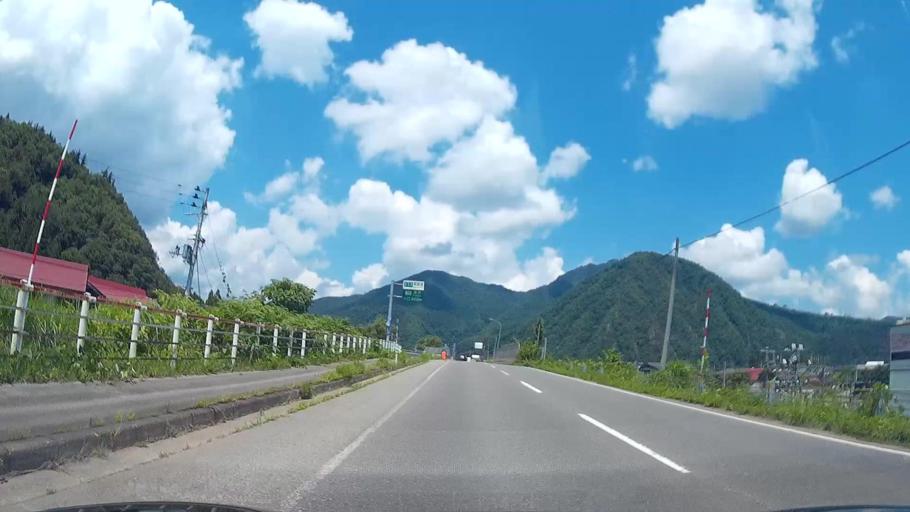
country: JP
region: Niigata
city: Shiozawa
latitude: 36.9265
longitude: 138.8239
